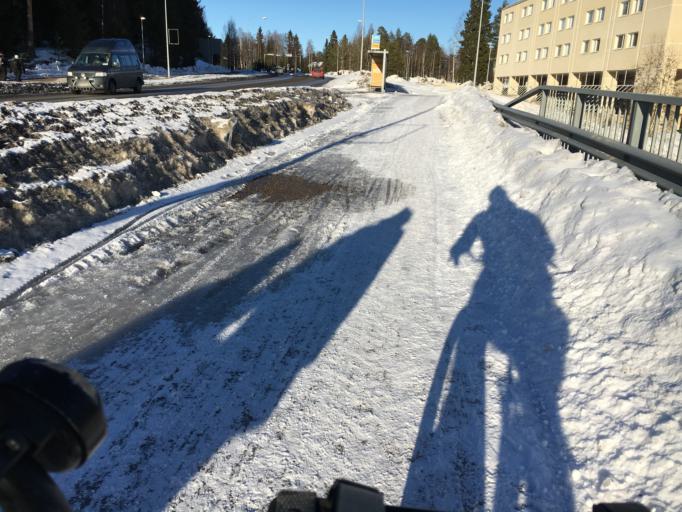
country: FI
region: Kainuu
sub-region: Kajaani
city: Kajaani
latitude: 64.2261
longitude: 27.7393
